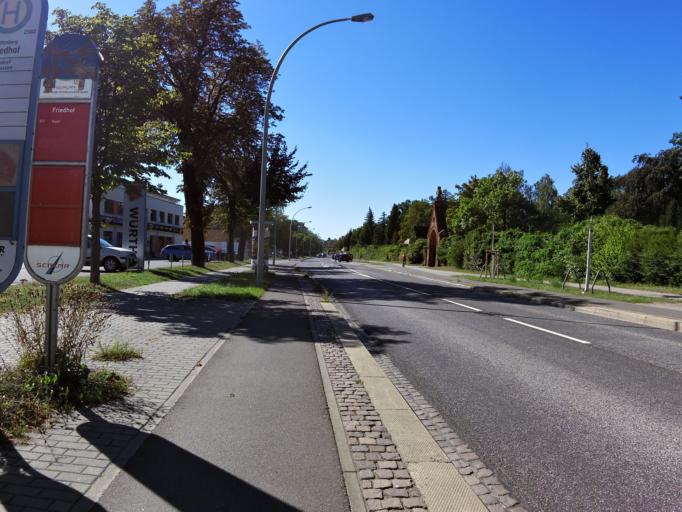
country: DE
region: Saxony-Anhalt
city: Wittenburg
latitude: 51.8639
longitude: 12.6652
